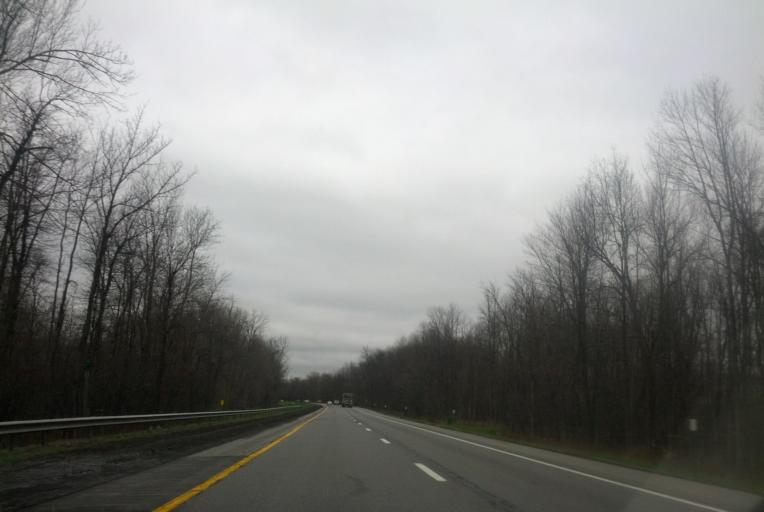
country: US
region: New York
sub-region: Ontario County
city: Shortsville
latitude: 42.9757
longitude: -77.1878
